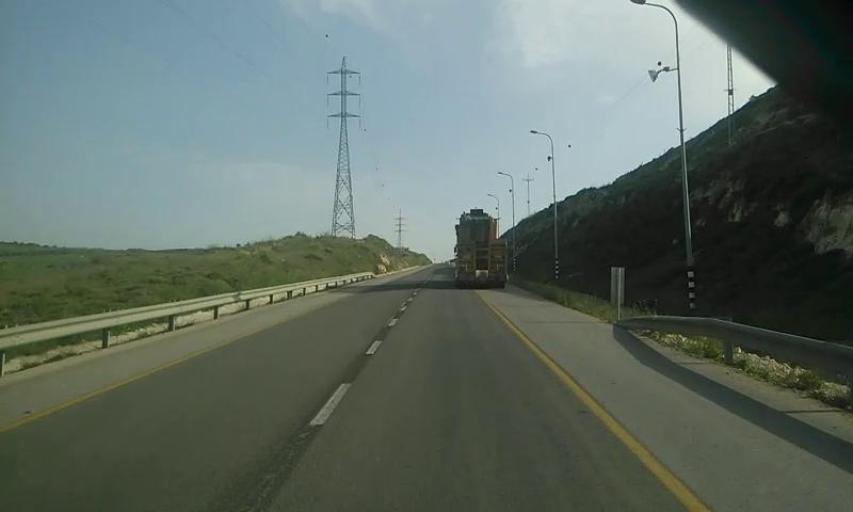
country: PS
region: West Bank
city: Sarrah
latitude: 32.2021
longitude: 35.1846
